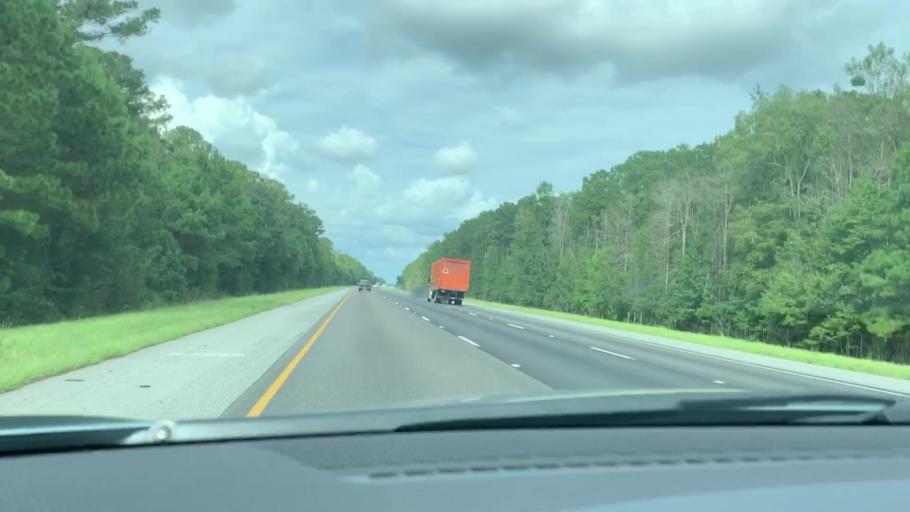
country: US
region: Georgia
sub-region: Liberty County
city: Midway
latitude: 31.6995
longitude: -81.3909
